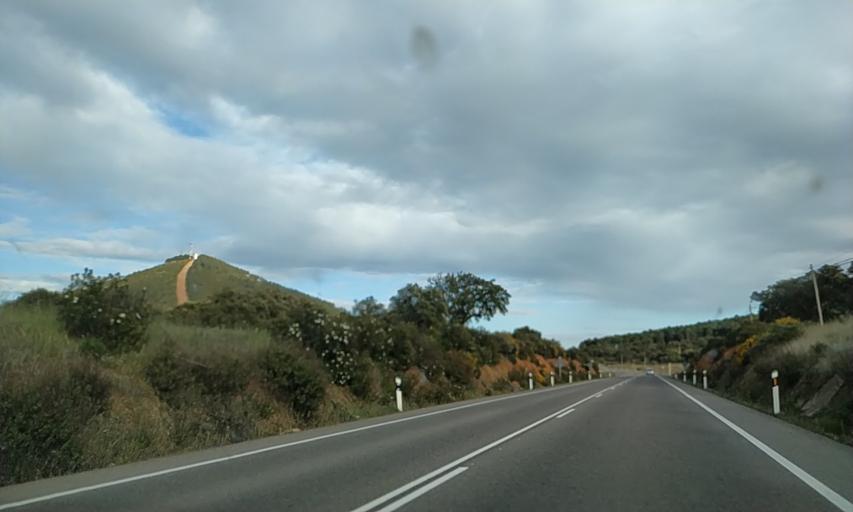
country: ES
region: Extremadura
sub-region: Provincia de Caceres
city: Canaveral
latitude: 39.8245
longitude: -6.3725
